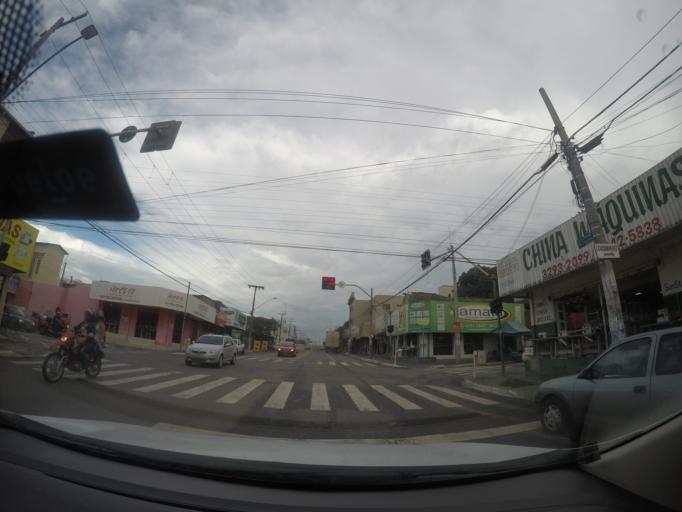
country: BR
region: Goias
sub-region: Goiania
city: Goiania
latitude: -16.6676
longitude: -49.2955
